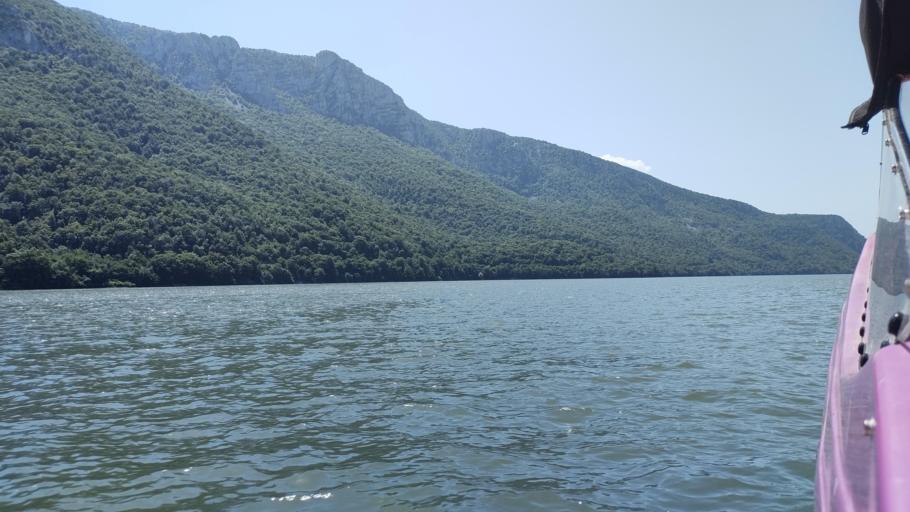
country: RO
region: Mehedinti
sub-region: Comuna Dubova
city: Dubova
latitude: 44.6096
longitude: 22.2706
